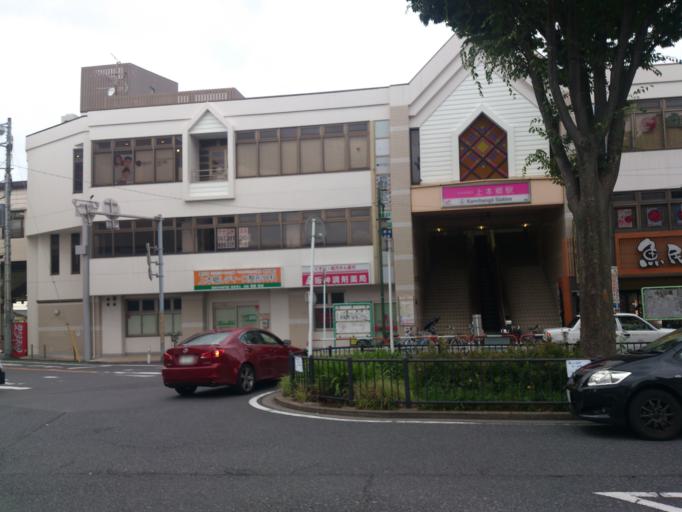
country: JP
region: Chiba
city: Matsudo
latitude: 35.7894
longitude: 139.9168
